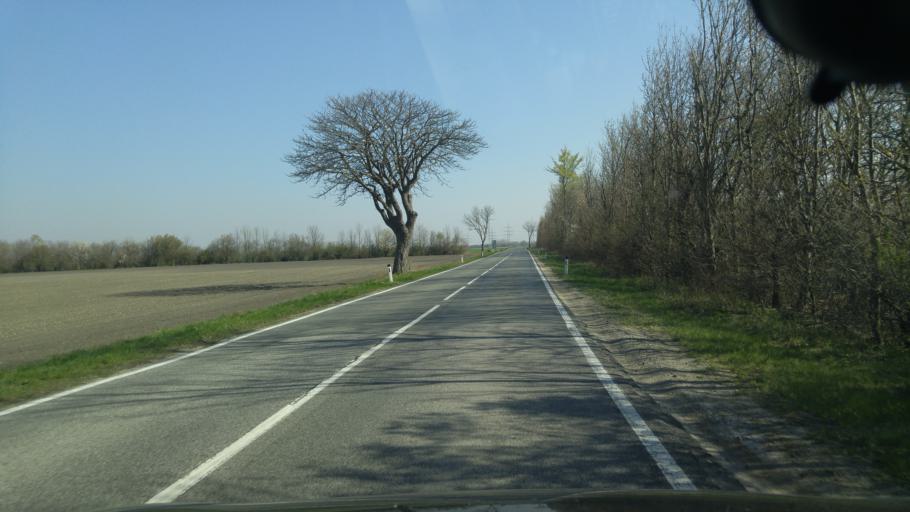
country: AT
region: Lower Austria
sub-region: Politischer Bezirk Baden
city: Trumau
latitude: 47.9965
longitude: 16.3671
